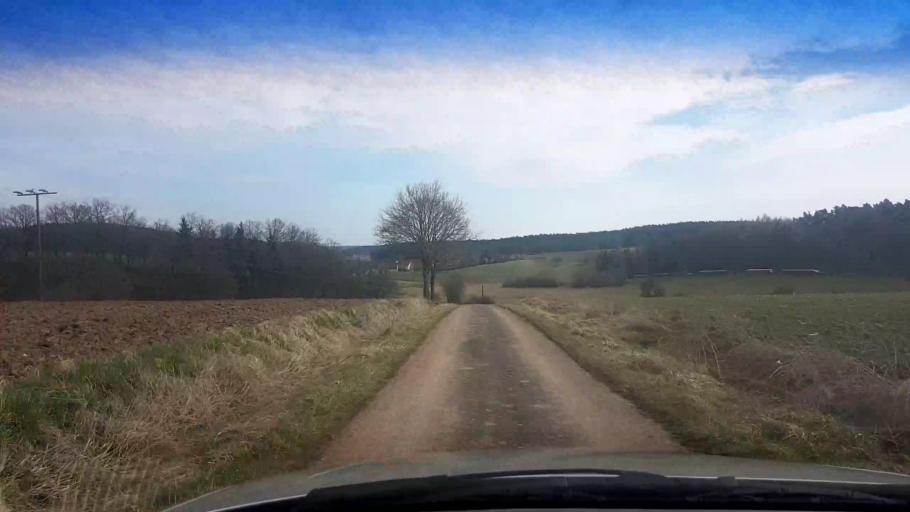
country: DE
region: Bavaria
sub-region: Upper Franconia
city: Burgebrach
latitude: 49.8017
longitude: 10.7572
